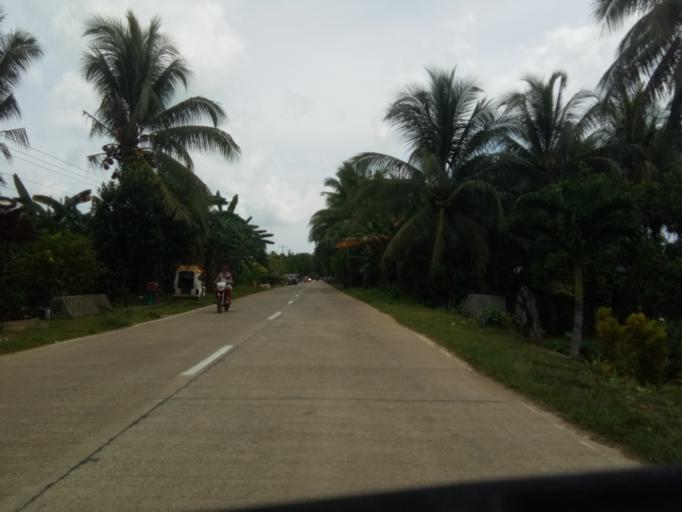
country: PH
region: Caraga
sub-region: Province of Surigao del Norte
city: San Isidro
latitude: 9.9285
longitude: 126.0577
